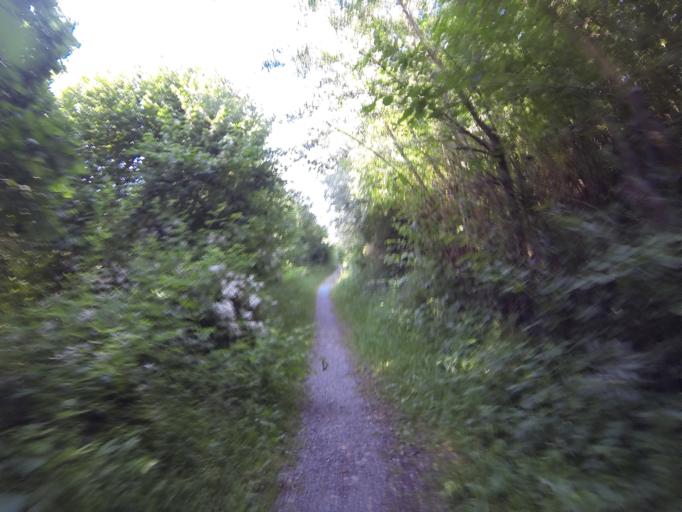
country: CH
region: Lucerne
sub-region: Lucerne-Land District
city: Ebikon
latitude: 47.0875
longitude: 8.3243
